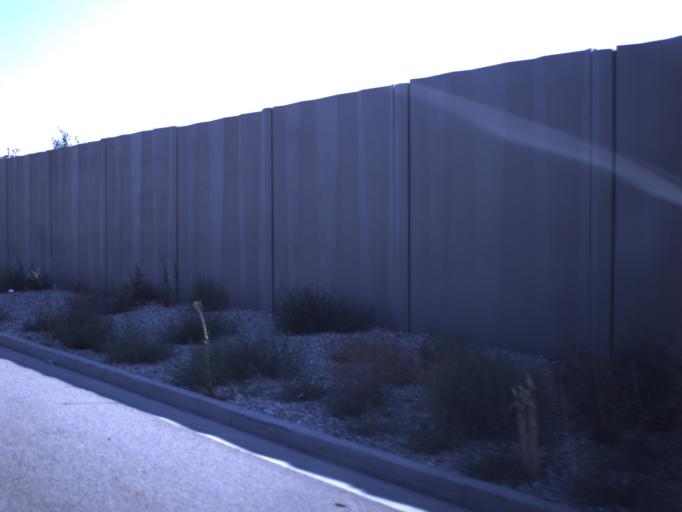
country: US
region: Utah
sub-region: Salt Lake County
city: Herriman
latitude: 40.5252
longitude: -112.0054
